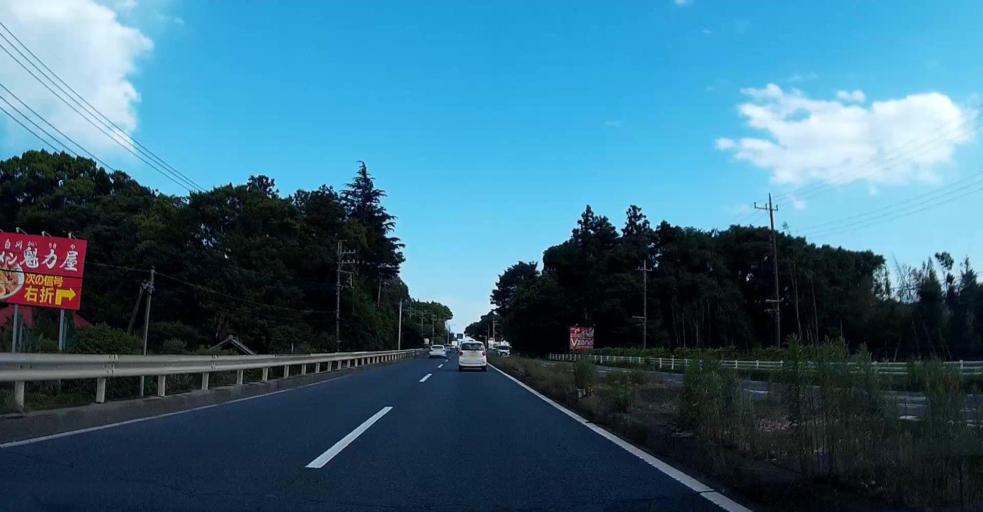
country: JP
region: Chiba
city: Shiroi
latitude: 35.8105
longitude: 140.0347
